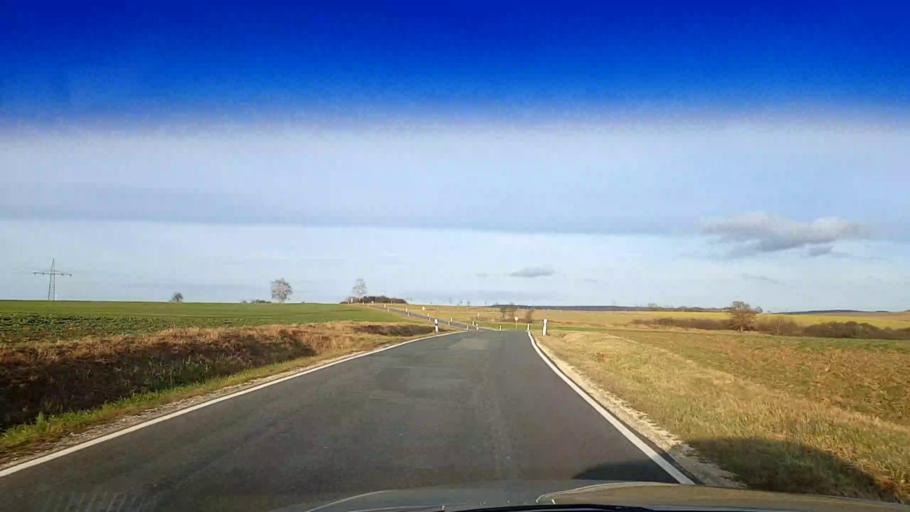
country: DE
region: Bavaria
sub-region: Upper Franconia
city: Strullendorf
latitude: 49.8466
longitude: 11.0010
